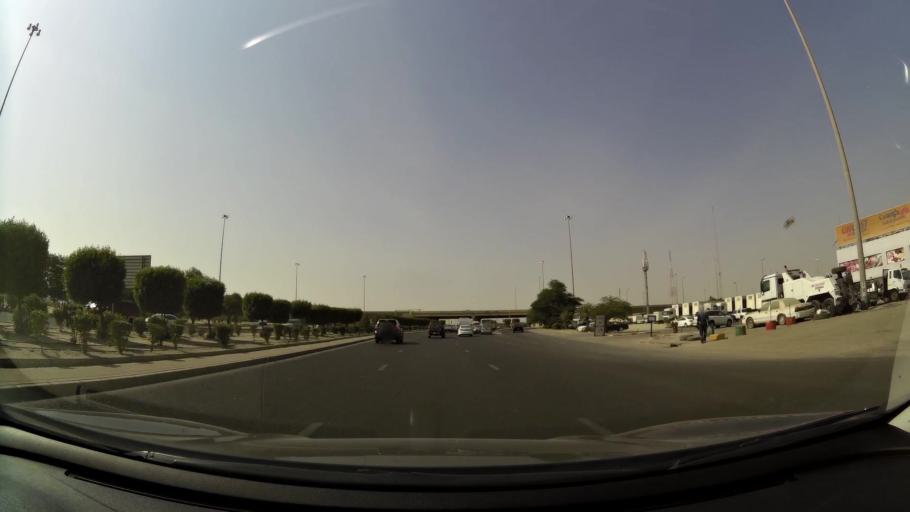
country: KW
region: Al Ahmadi
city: Al Fahahil
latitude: 29.0715
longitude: 48.1136
